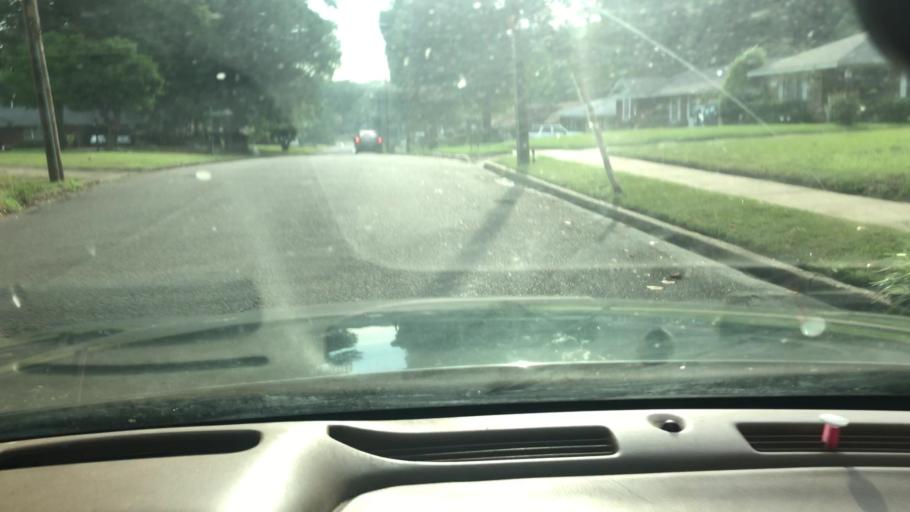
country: US
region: Tennessee
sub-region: Shelby County
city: New South Memphis
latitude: 35.0466
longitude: -90.0162
